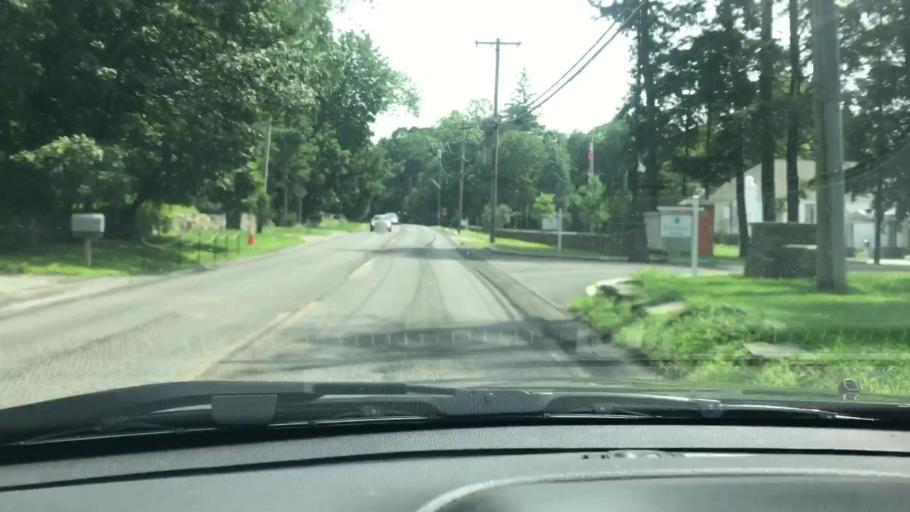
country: US
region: New York
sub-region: Westchester County
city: Bedford
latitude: 41.2184
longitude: -73.6571
